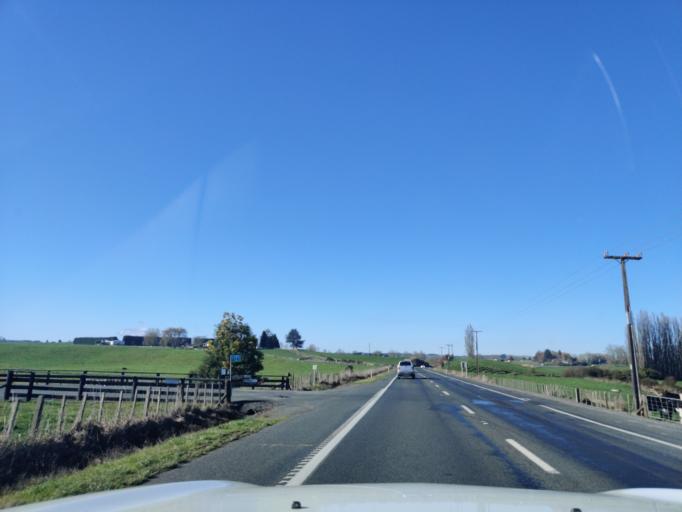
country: NZ
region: Waikato
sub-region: Matamata-Piako District
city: Matamata
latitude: -38.0251
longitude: 175.7869
